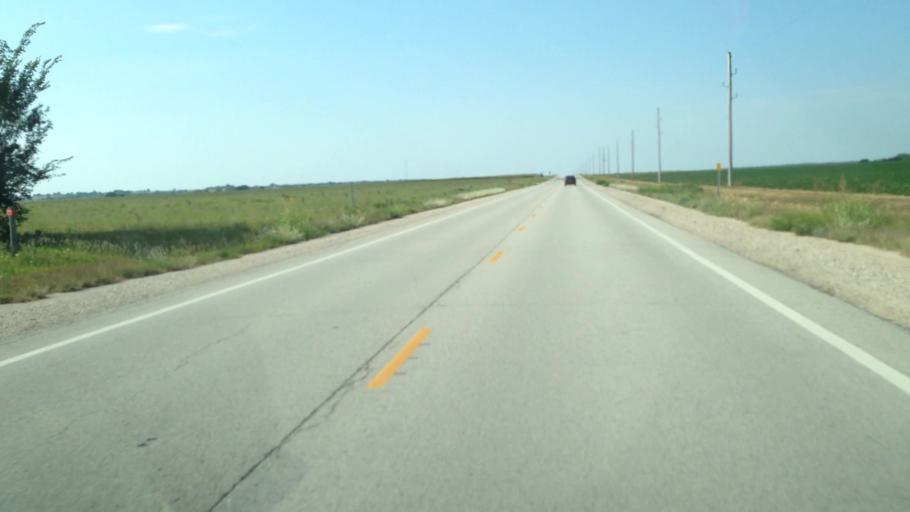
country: US
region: Kansas
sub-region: Anderson County
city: Garnett
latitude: 38.0473
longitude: -95.1696
